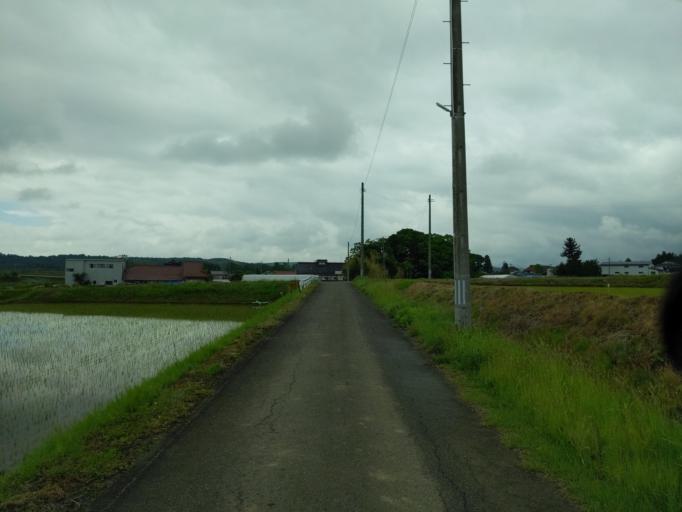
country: JP
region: Fukushima
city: Koriyama
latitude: 37.3514
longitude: 140.2783
